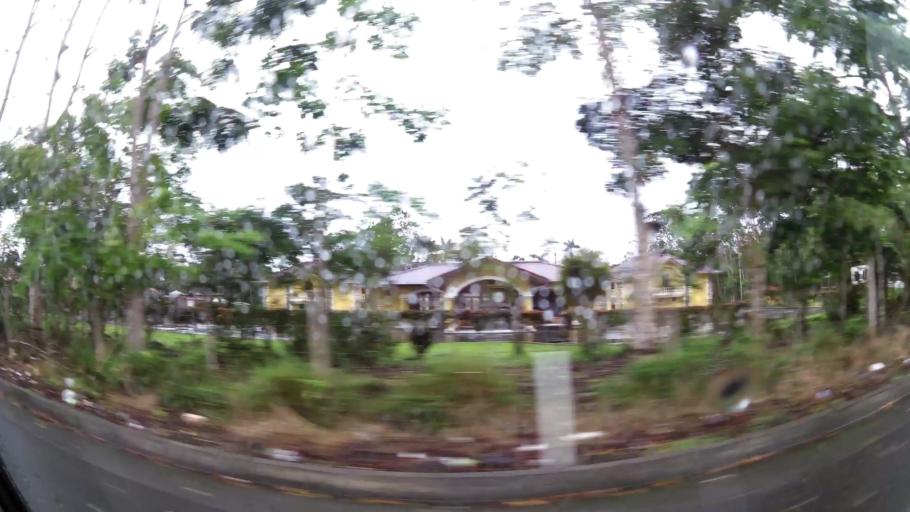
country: EC
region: Santo Domingo de los Tsachilas
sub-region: Canton Santo Domingo de los Colorados
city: Santo Domingo de los Colorados
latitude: -0.2348
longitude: -79.1339
